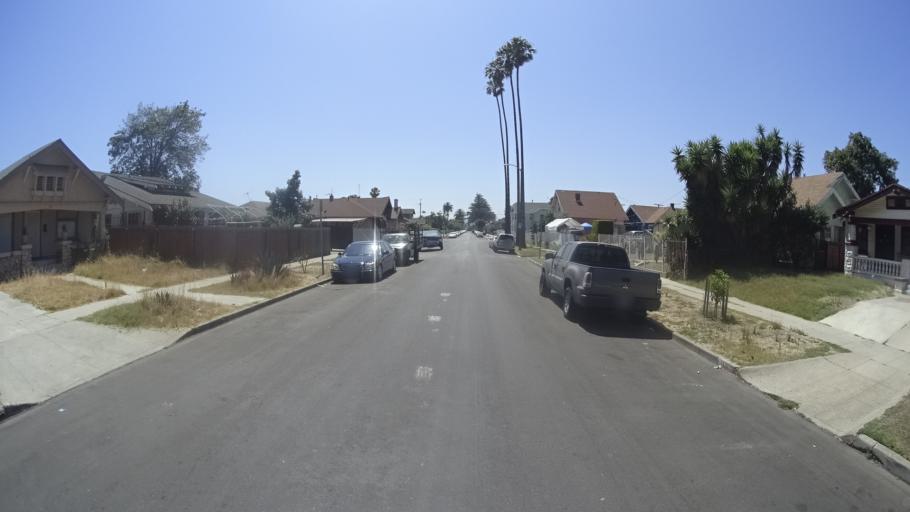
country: US
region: California
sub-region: Los Angeles County
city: View Park-Windsor Hills
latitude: 33.9987
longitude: -118.2949
